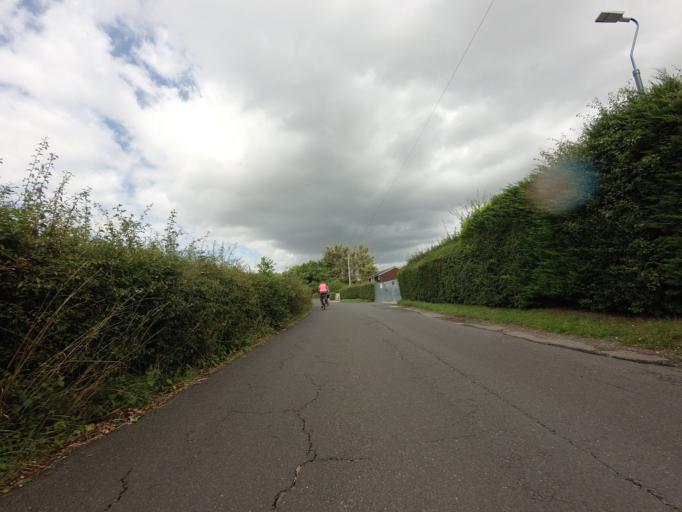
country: GB
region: England
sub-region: Kent
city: Sevenoaks
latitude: 51.2964
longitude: 0.1773
